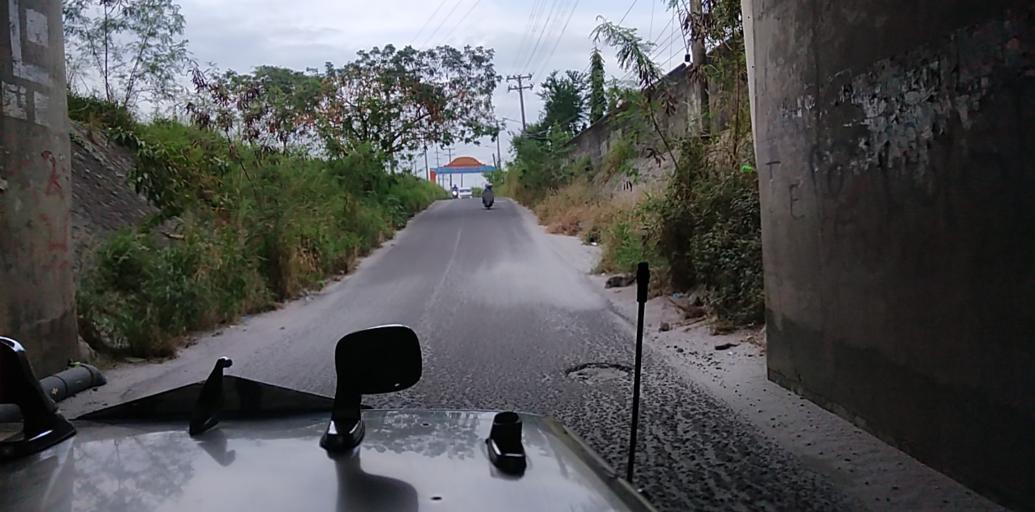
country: PH
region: Central Luzon
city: Santol
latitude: 15.1627
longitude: 120.5482
